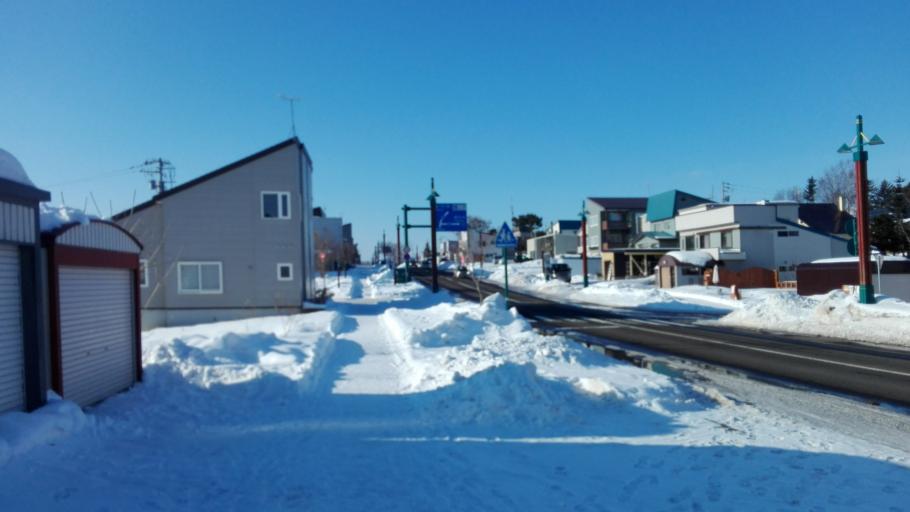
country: JP
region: Hokkaido
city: Niseko Town
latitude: 42.8027
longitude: 140.6898
